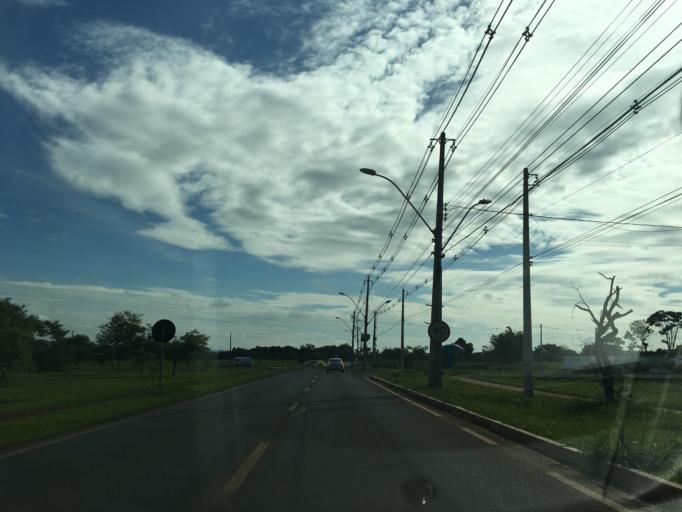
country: BR
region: Federal District
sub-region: Brasilia
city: Brasilia
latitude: -15.8675
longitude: -47.9416
